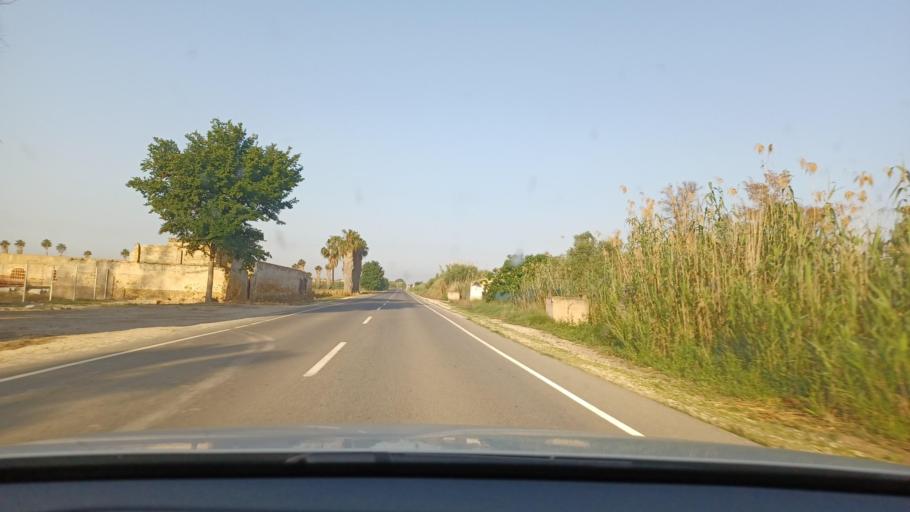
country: ES
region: Valencia
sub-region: Provincia de Alicante
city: Daya Vieja
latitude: 38.1473
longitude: -0.7232
